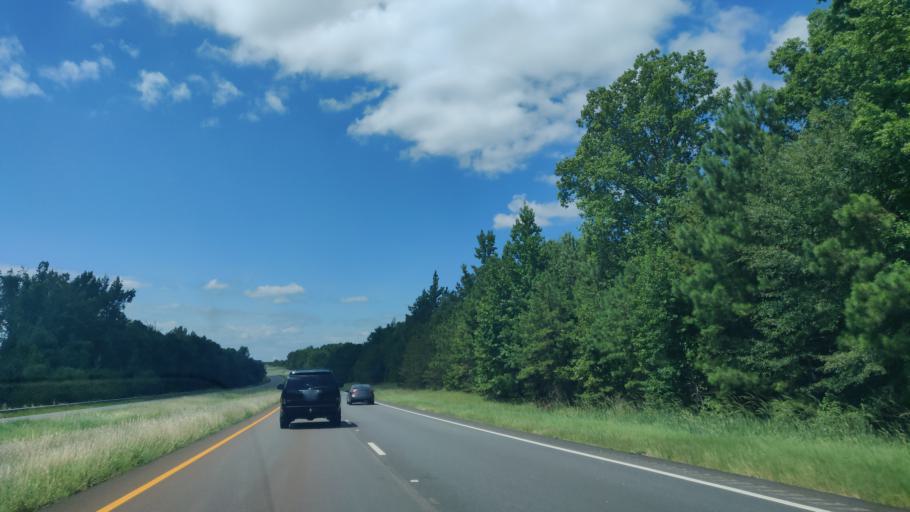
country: US
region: Georgia
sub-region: Stewart County
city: Richland
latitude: 32.0965
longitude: -84.6733
